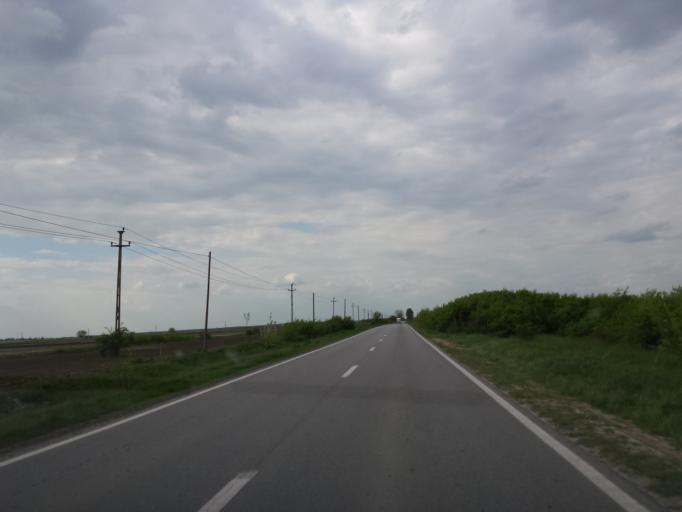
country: RO
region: Timis
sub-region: Oras Sannicolau Mare
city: Sannicolau Mare
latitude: 46.0994
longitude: 20.5998
